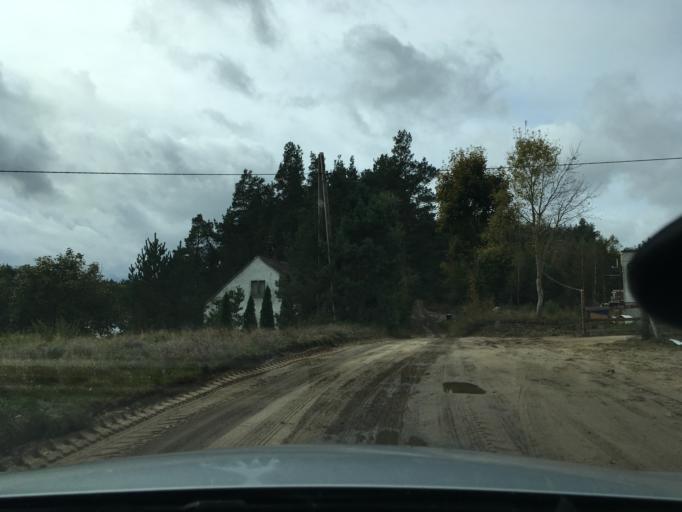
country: PL
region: Pomeranian Voivodeship
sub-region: Powiat koscierski
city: Koscierzyna
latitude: 54.1087
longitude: 18.0225
